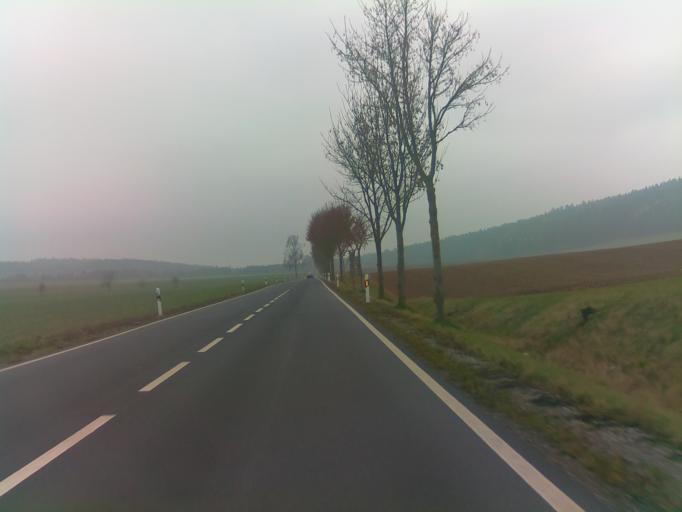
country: DE
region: Thuringia
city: Romhild
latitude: 50.4471
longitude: 10.5441
